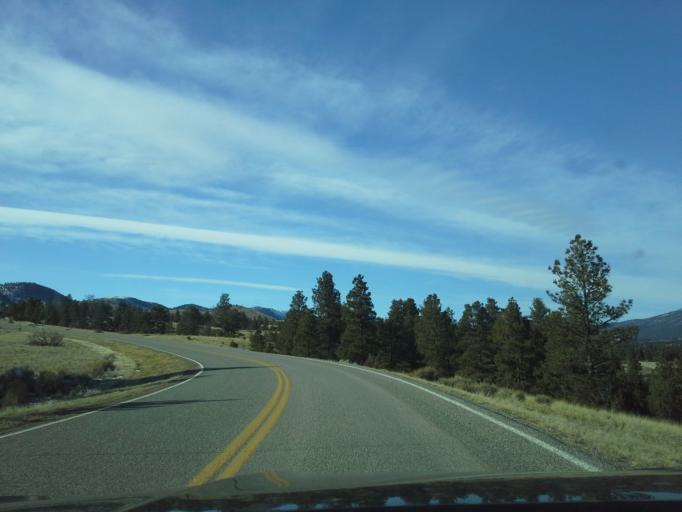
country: US
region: Montana
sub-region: Lewis and Clark County
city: Helena Valley Northeast
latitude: 46.8227
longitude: -111.9768
